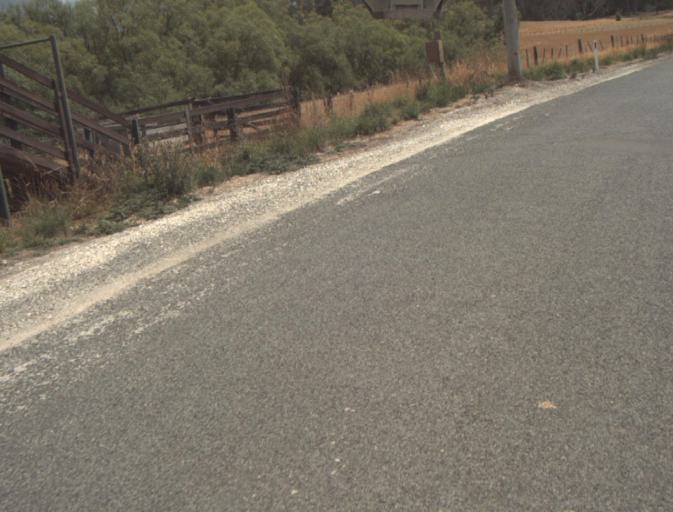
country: AU
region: Tasmania
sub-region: Launceston
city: Mayfield
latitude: -41.2245
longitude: 147.1376
